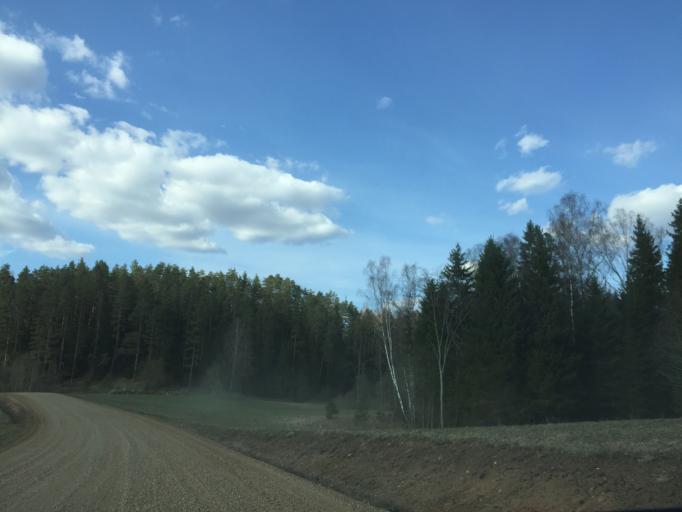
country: EE
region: Tartu
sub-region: Elva linn
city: Elva
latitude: 58.1000
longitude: 26.5075
